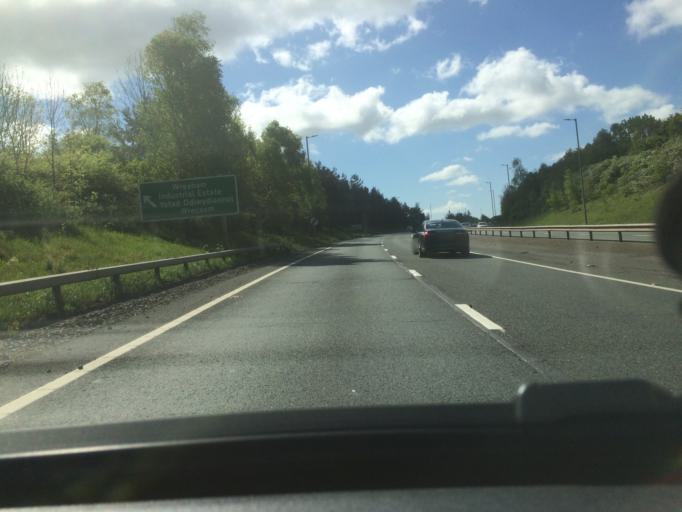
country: GB
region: Wales
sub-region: Wrexham
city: Gresford
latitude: 53.0801
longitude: -2.9865
